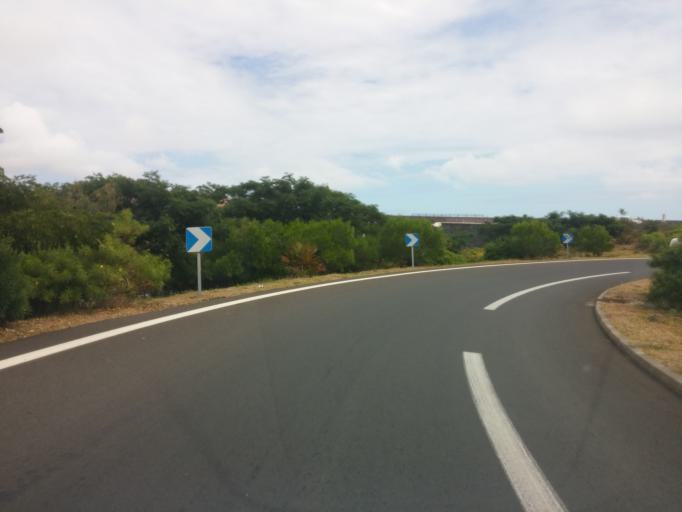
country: RE
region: Reunion
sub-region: Reunion
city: Saint-Paul
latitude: -21.0214
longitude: 55.2573
